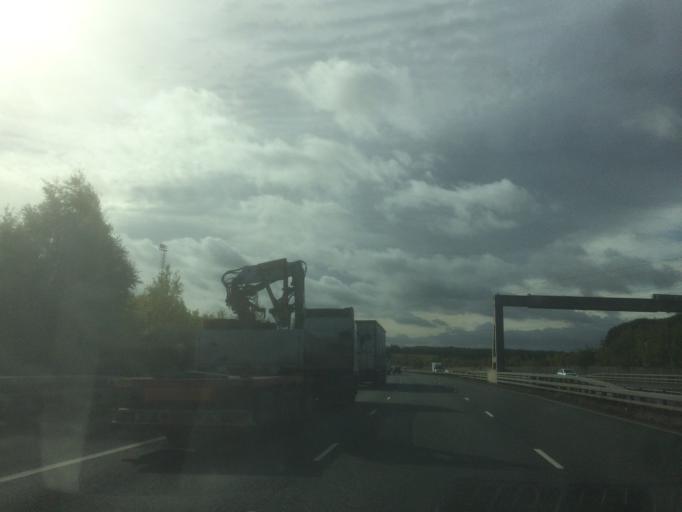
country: GB
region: England
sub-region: City and Borough of Wakefield
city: Ferrybridge
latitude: 53.7329
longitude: -1.2872
